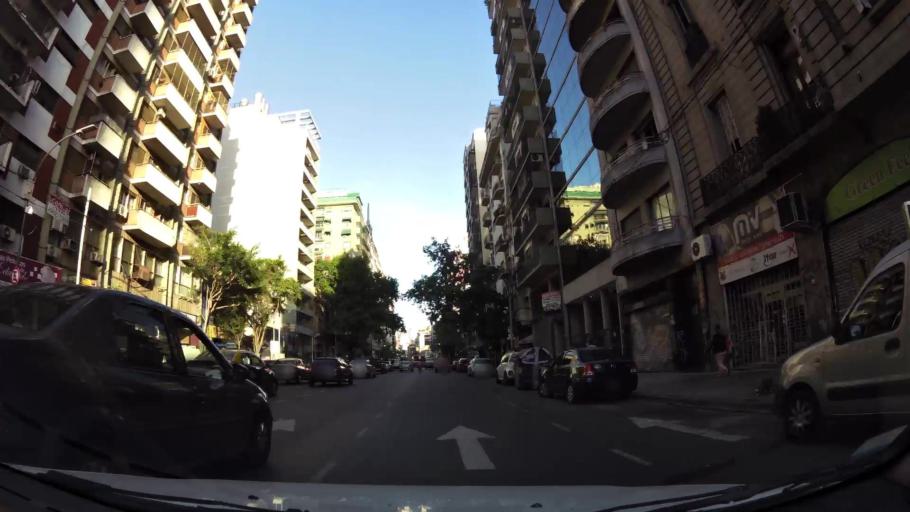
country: AR
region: Buenos Aires F.D.
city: Buenos Aires
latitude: -34.6043
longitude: -58.4076
